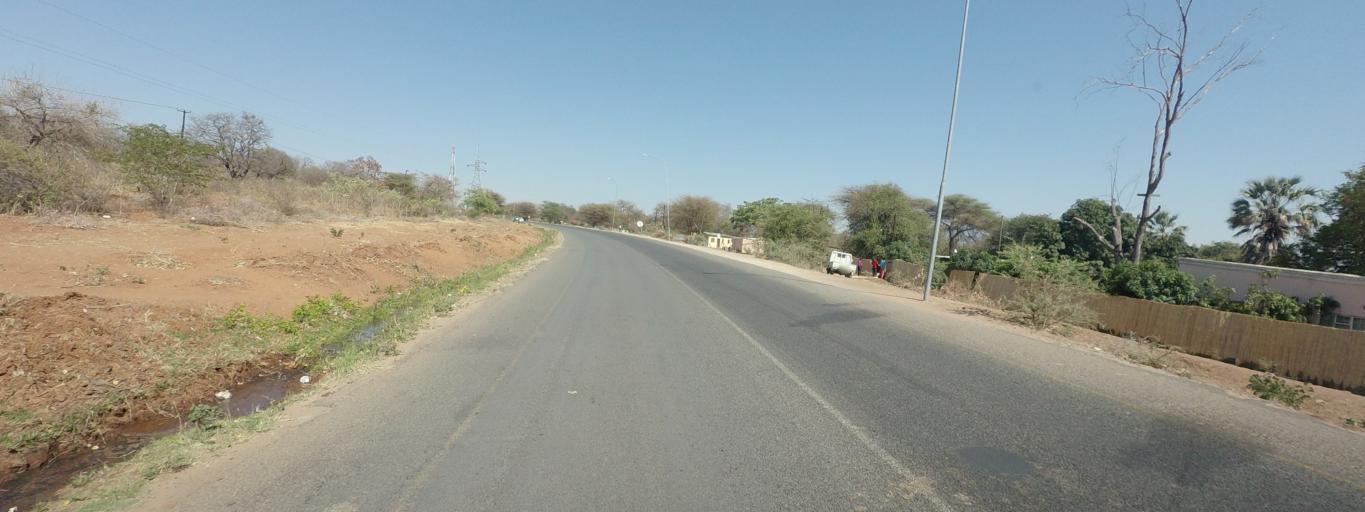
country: BW
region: North West
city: Kasane
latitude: -17.7987
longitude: 25.2355
